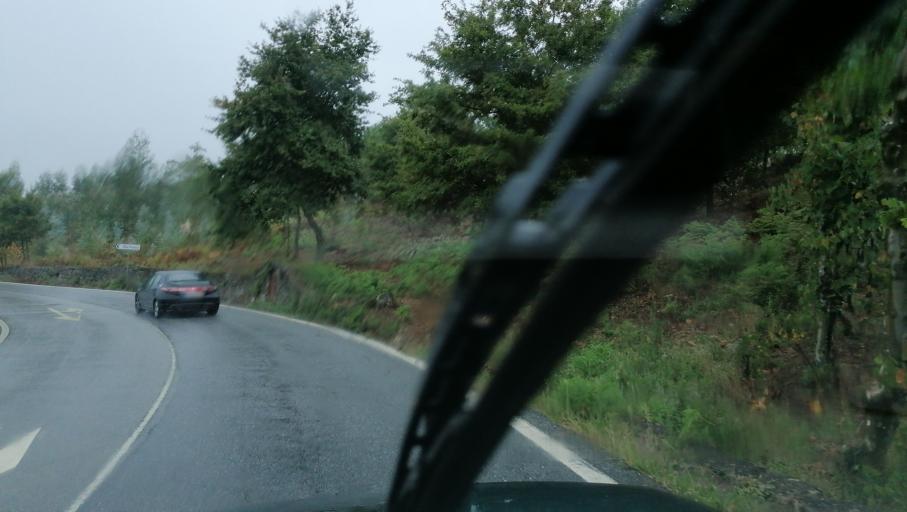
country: PT
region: Braga
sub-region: Cabeceiras de Basto
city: Cabeceiras de Basto
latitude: 41.4997
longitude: -7.9043
